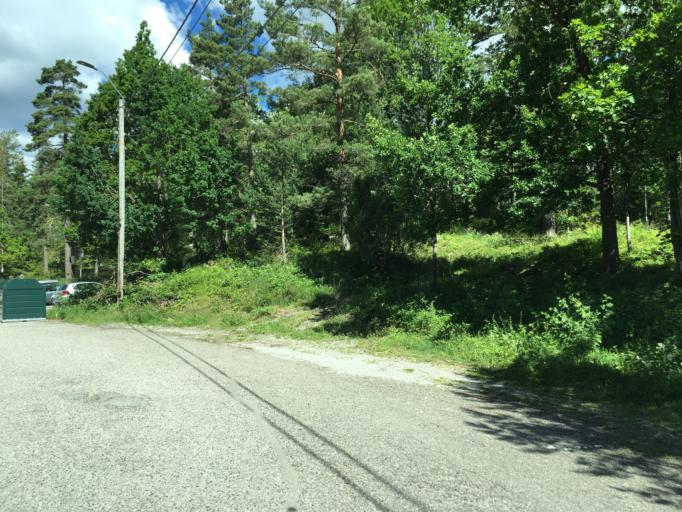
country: NO
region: Buskerud
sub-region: Drammen
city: Drammen
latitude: 59.7528
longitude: 10.2034
